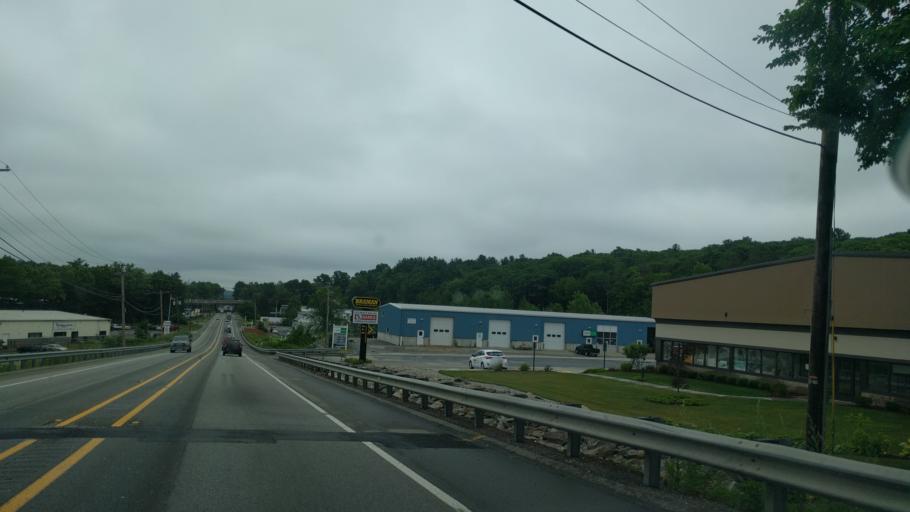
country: US
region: Massachusetts
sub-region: Worcester County
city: Auburn
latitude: 42.2001
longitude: -71.8172
